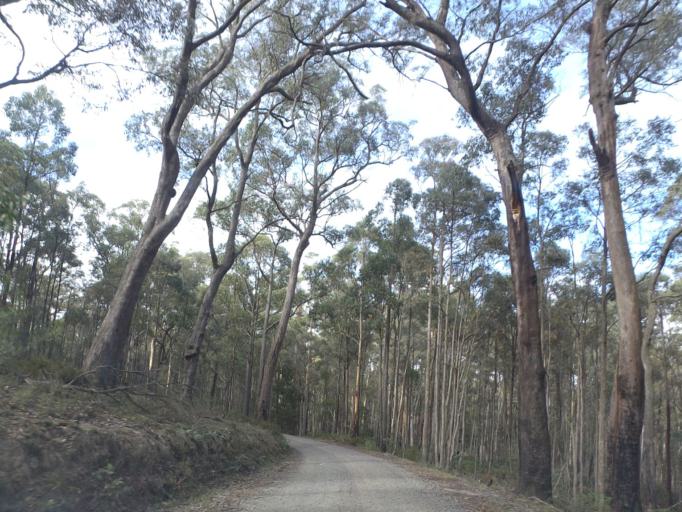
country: AU
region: Victoria
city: Brown Hill
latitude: -37.4915
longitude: 144.1744
